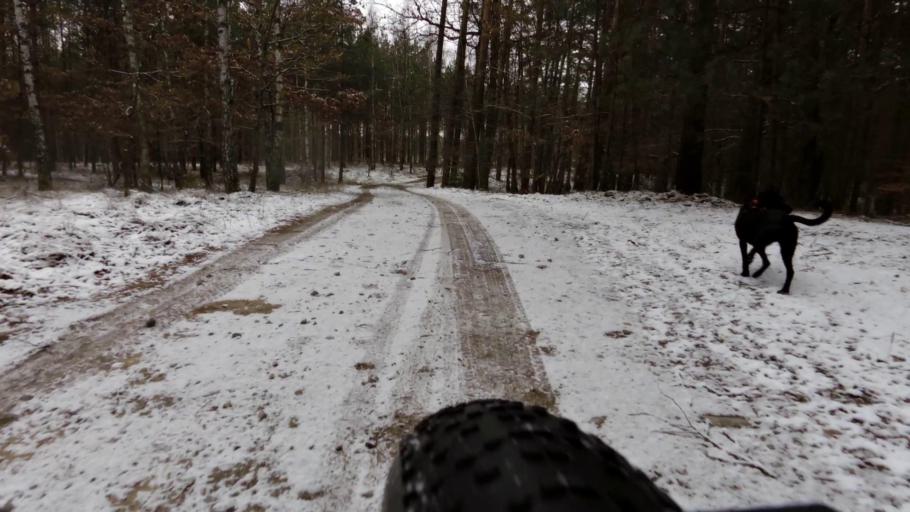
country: PL
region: West Pomeranian Voivodeship
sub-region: Powiat walecki
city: Miroslawiec
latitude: 53.2956
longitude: 16.0628
